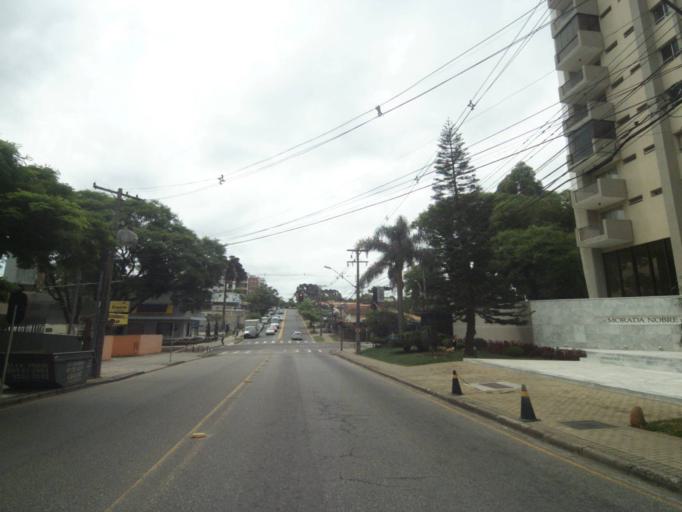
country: BR
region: Parana
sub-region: Curitiba
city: Curitiba
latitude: -25.4320
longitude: -49.2993
